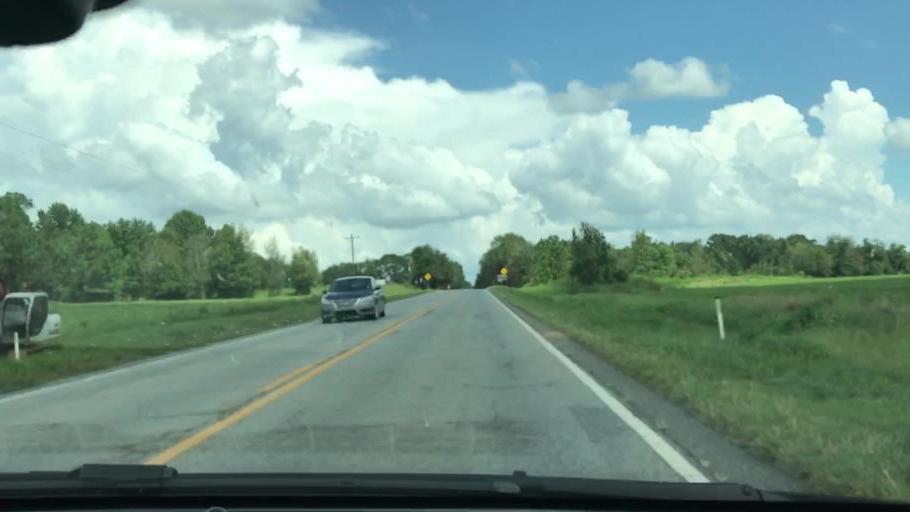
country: US
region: Georgia
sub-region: Seminole County
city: Donalsonville
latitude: 30.9818
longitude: -84.9784
